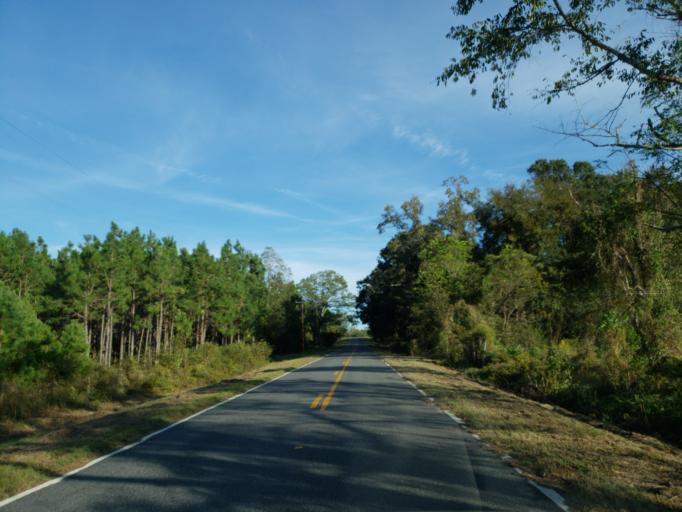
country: US
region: Georgia
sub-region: Crisp County
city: Cordele
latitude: 32.0306
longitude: -83.7469
